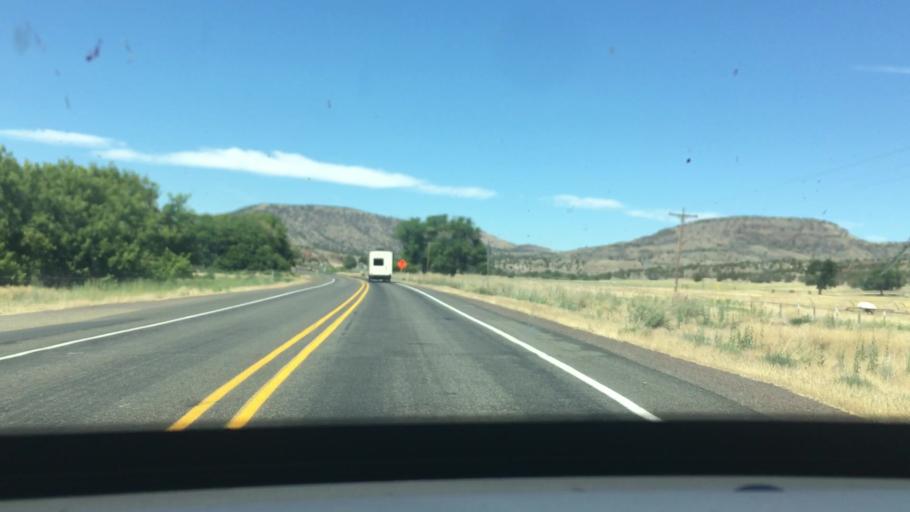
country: US
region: Oregon
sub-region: Jefferson County
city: Madras
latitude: 44.8063
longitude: -120.9350
